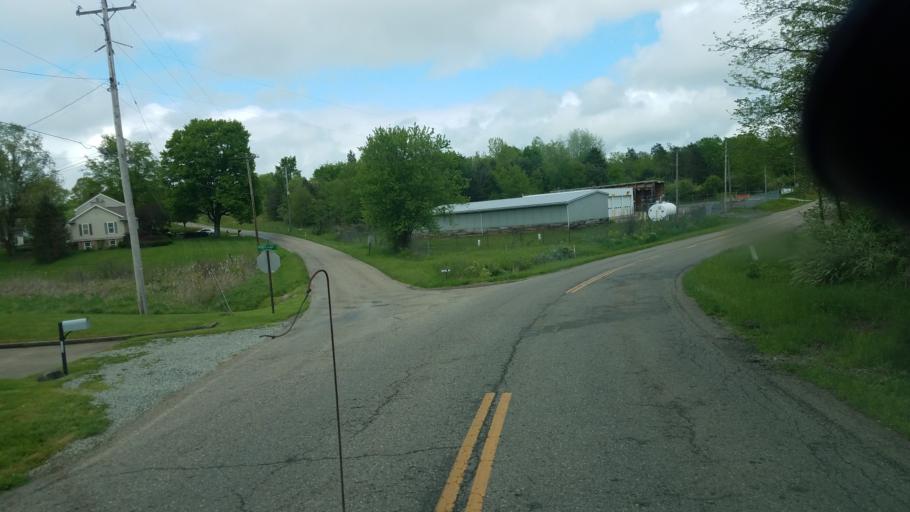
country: US
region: Ohio
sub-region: Tuscarawas County
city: Strasburg
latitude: 40.6189
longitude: -81.4210
